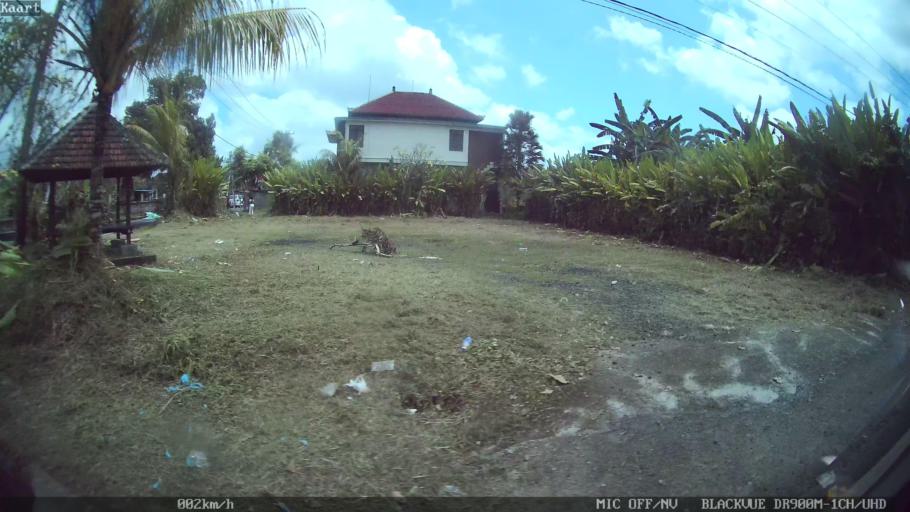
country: ID
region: Bali
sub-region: Kabupaten Gianyar
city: Ubud
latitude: -8.5401
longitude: 115.2816
